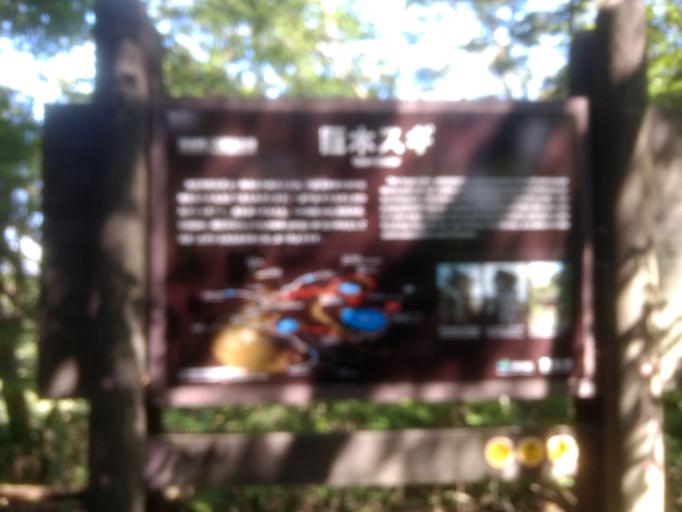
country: JP
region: Miyazaki
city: Kobayashi
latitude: 31.9583
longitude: 130.8457
